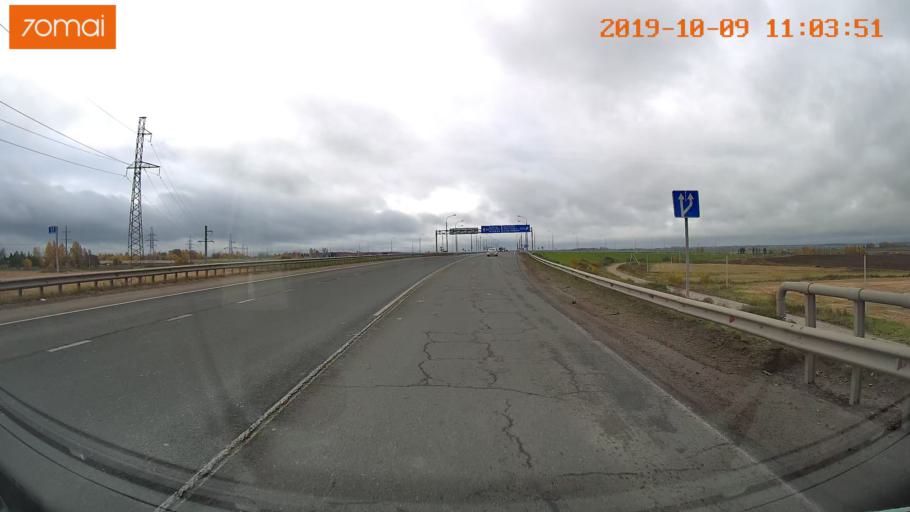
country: RU
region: Vologda
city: Vologda
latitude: 59.2182
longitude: 39.7736
